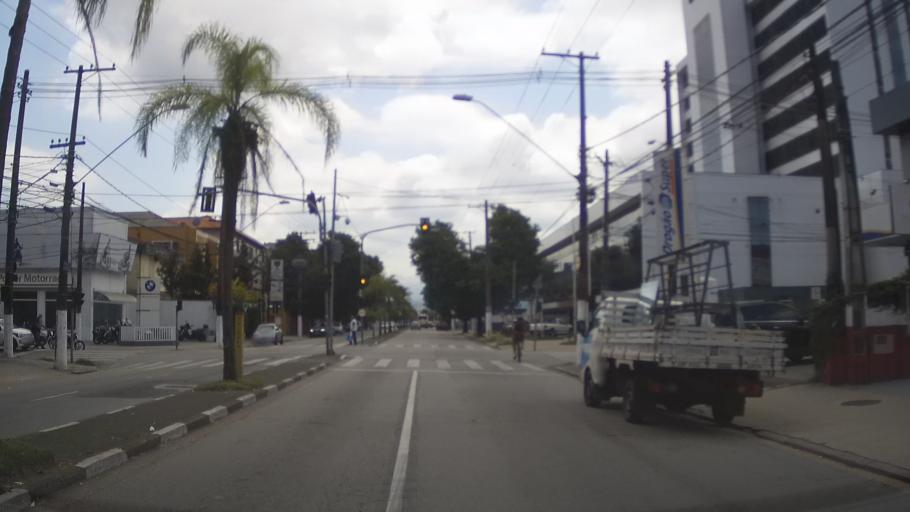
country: BR
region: Sao Paulo
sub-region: Santos
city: Santos
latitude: -23.9521
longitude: -46.3223
